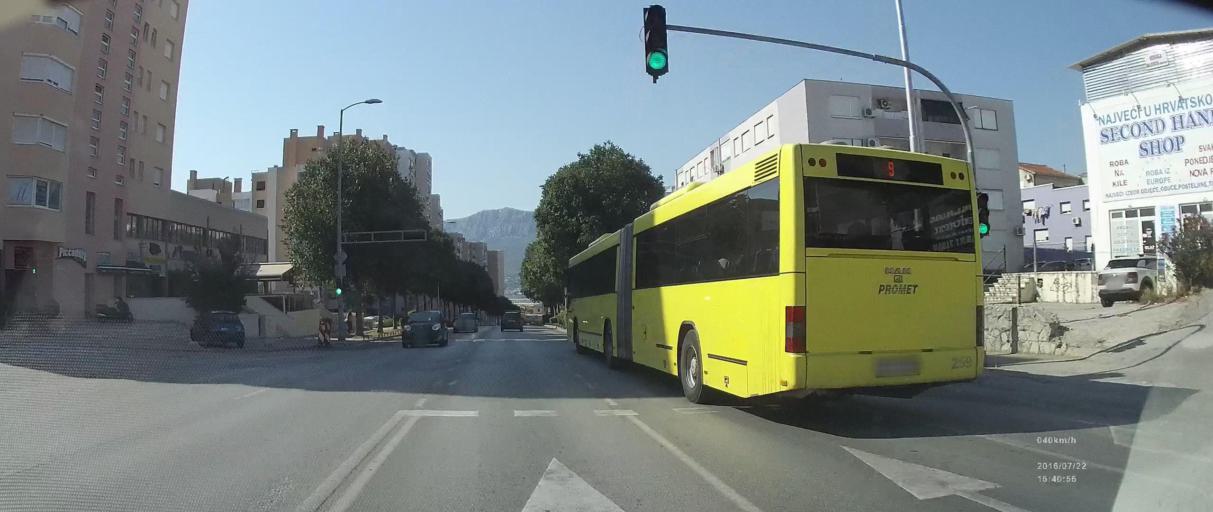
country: HR
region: Splitsko-Dalmatinska
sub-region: Grad Split
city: Split
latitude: 43.5164
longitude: 16.4515
